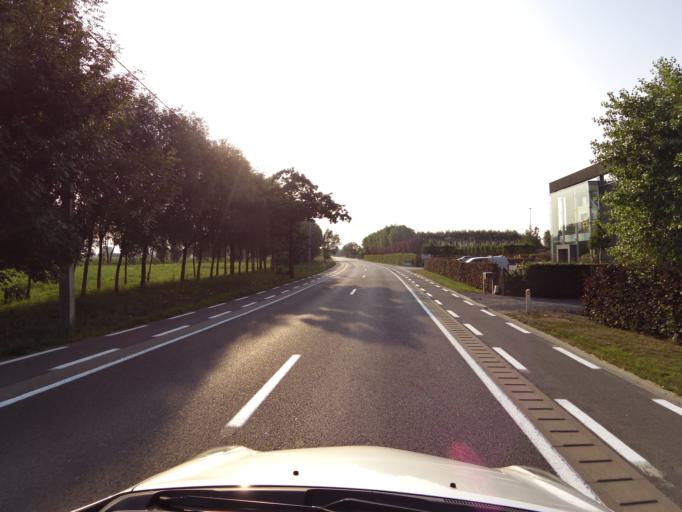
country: BE
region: Flanders
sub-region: Provincie West-Vlaanderen
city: Pittem
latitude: 50.9999
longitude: 3.2271
